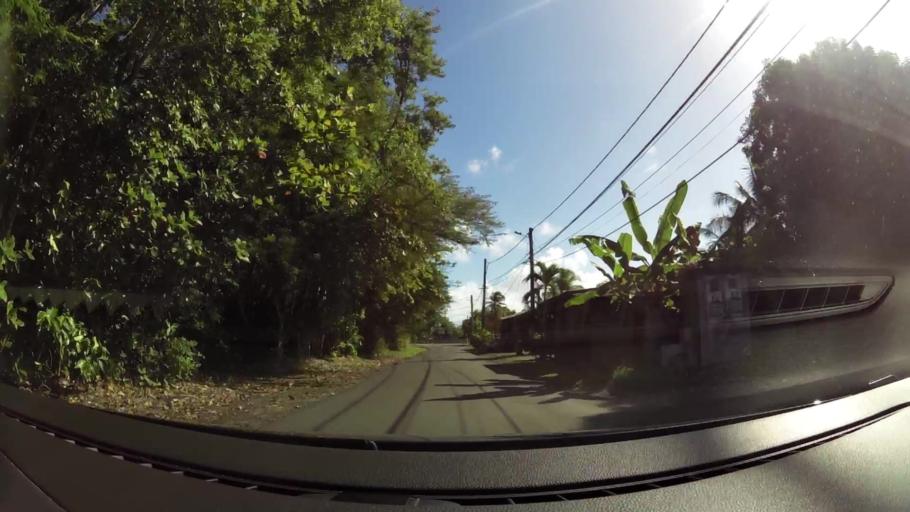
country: GP
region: Guadeloupe
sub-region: Guadeloupe
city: Sainte-Anne
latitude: 16.2280
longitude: -61.3757
